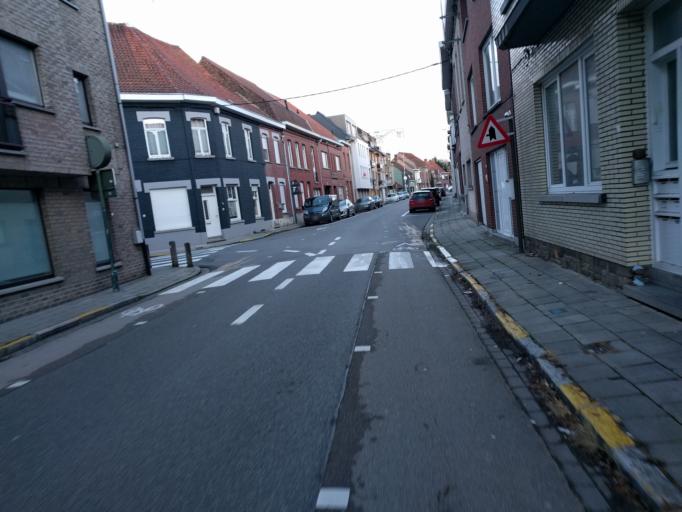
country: BE
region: Flanders
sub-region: Provincie West-Vlaanderen
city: Wevelgem
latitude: 50.8114
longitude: 3.1856
